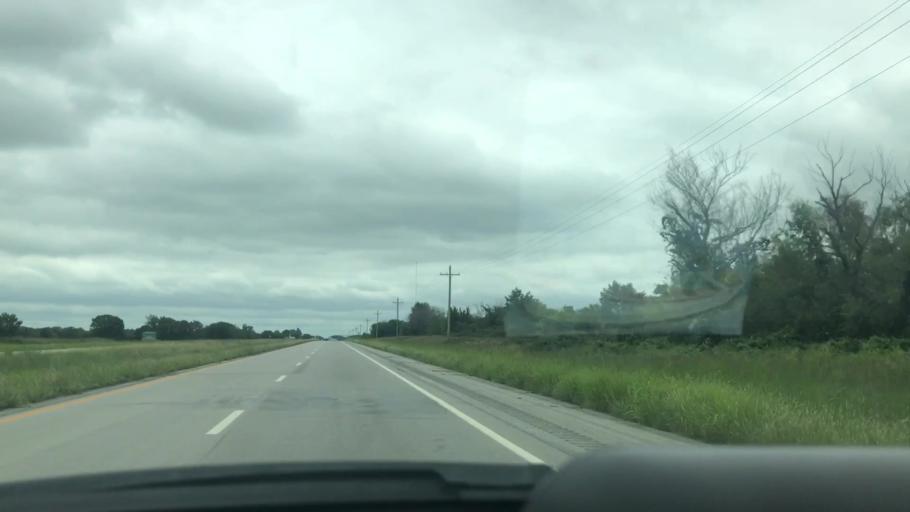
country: US
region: Oklahoma
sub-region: Mayes County
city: Pryor
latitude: 36.4120
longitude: -95.2818
